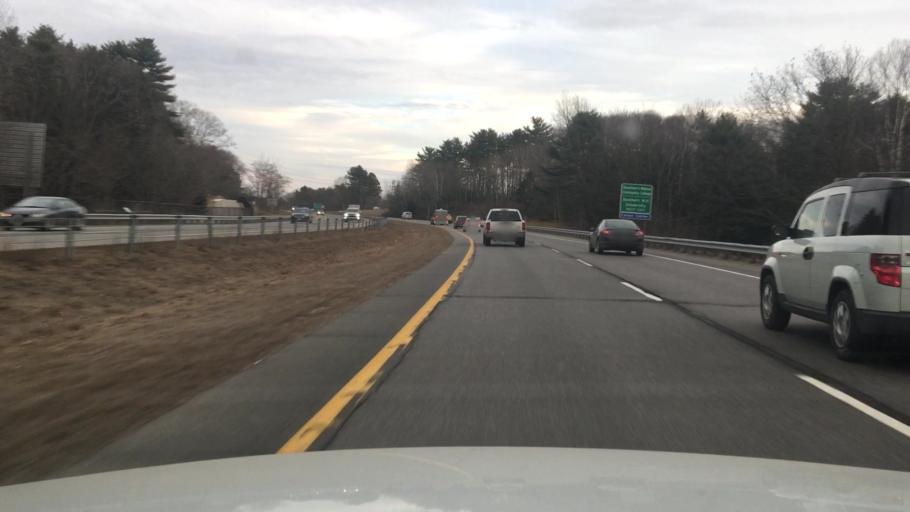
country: US
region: Maine
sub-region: Cumberland County
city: Brunswick
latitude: 43.9092
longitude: -69.9278
